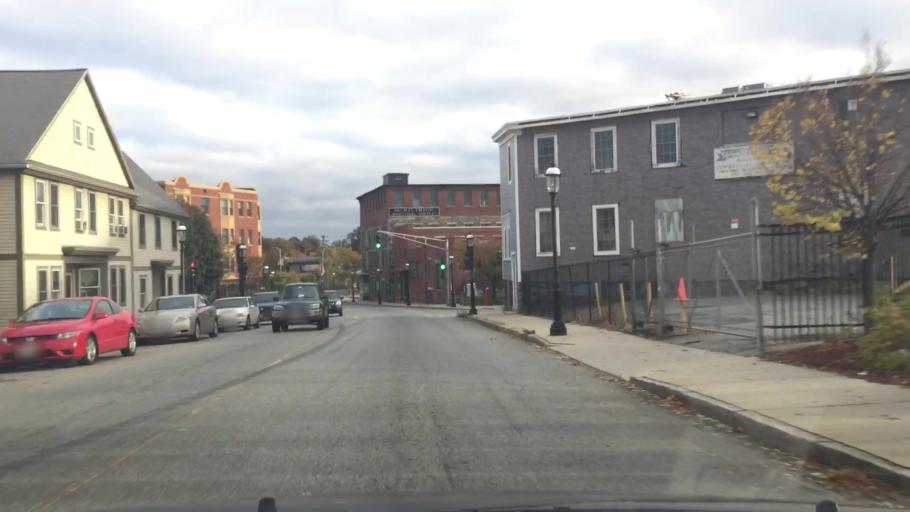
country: US
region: Massachusetts
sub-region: Middlesex County
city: Lowell
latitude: 42.6423
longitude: -71.3189
